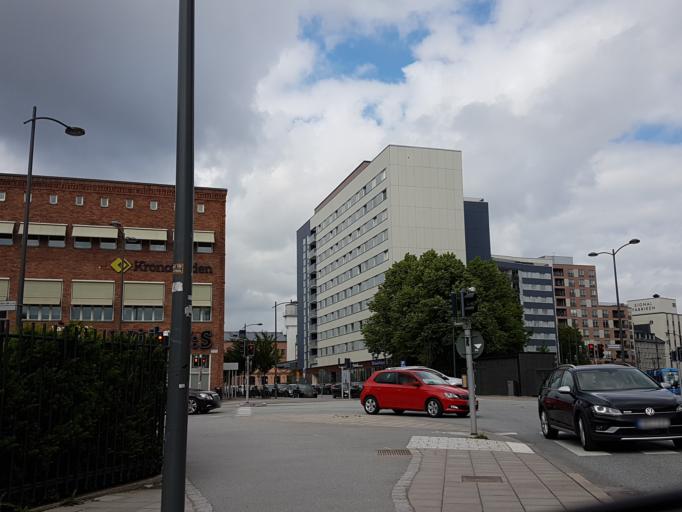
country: SE
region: Stockholm
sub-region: Sundbybergs Kommun
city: Sundbyberg
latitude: 59.3610
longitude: 17.9630
